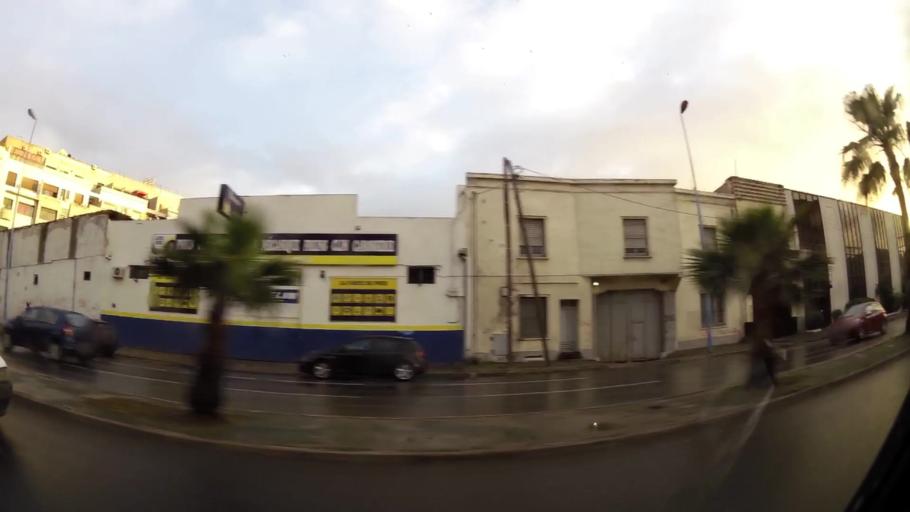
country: MA
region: Grand Casablanca
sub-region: Casablanca
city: Casablanca
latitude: 33.5877
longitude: -7.5980
